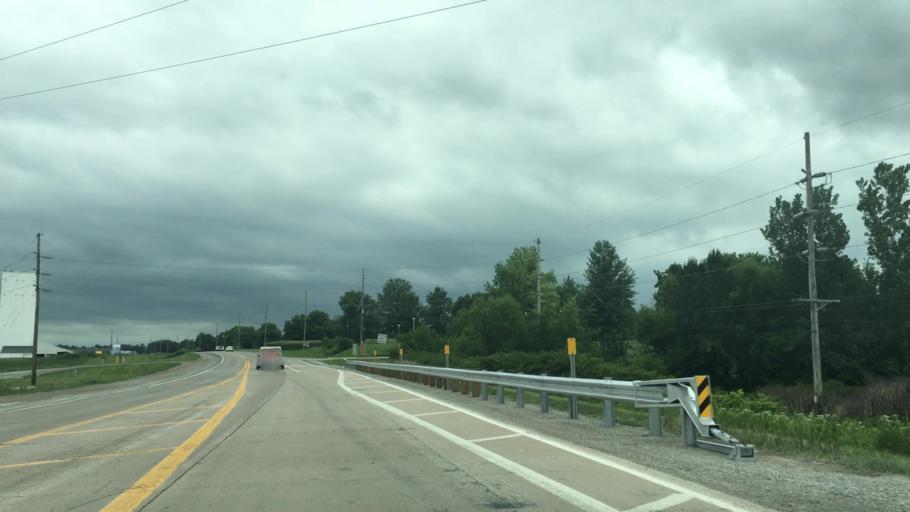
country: US
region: Iowa
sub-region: Johnson County
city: Tiffin
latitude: 41.7014
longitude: -91.6304
